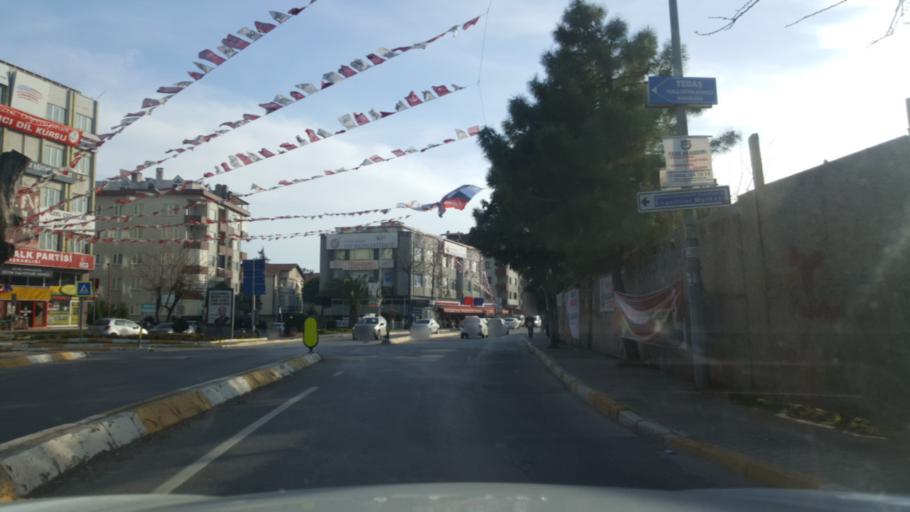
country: TR
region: Istanbul
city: Icmeler
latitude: 40.8222
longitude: 29.3095
